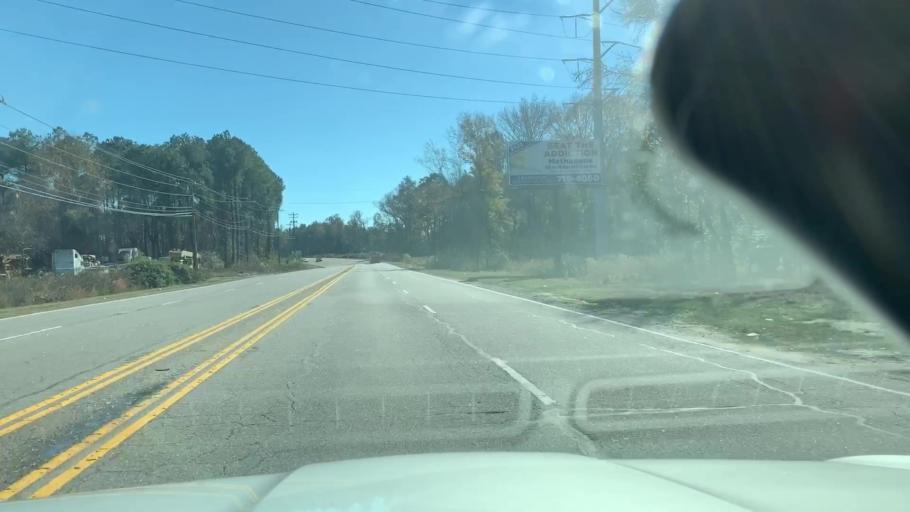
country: US
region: South Carolina
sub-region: Richland County
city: Columbia
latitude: 33.9426
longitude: -80.9853
